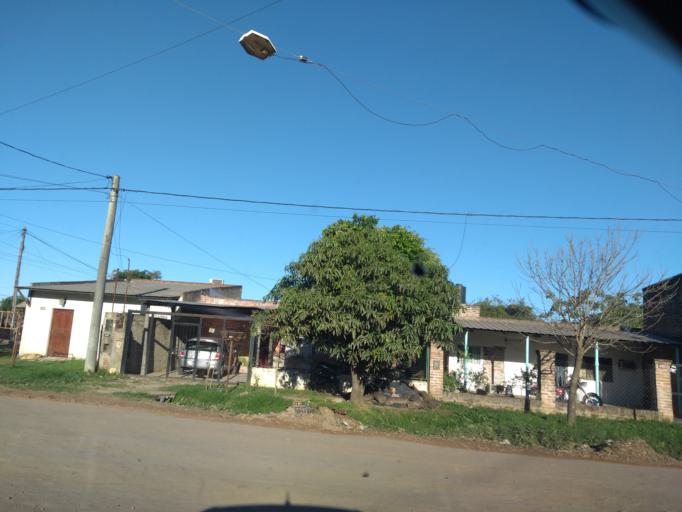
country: AR
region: Chaco
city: Barranqueras
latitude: -27.4885
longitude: -58.9426
